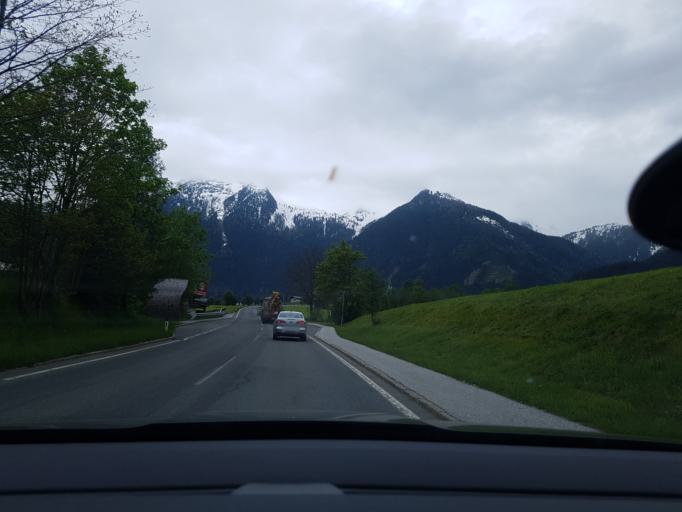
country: AT
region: Salzburg
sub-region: Politischer Bezirk Zell am See
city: Krimml
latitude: 47.2266
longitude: 12.1820
